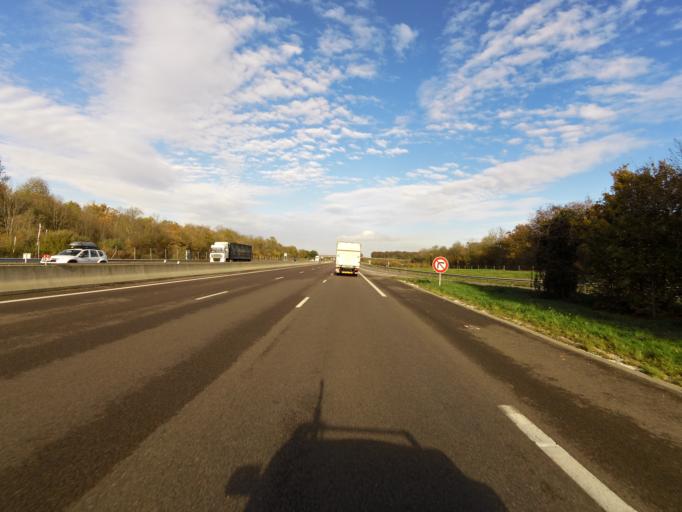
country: FR
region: Bourgogne
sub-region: Departement de la Cote-d'Or
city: Perrigny-les-Dijon
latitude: 47.2247
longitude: 5.0112
